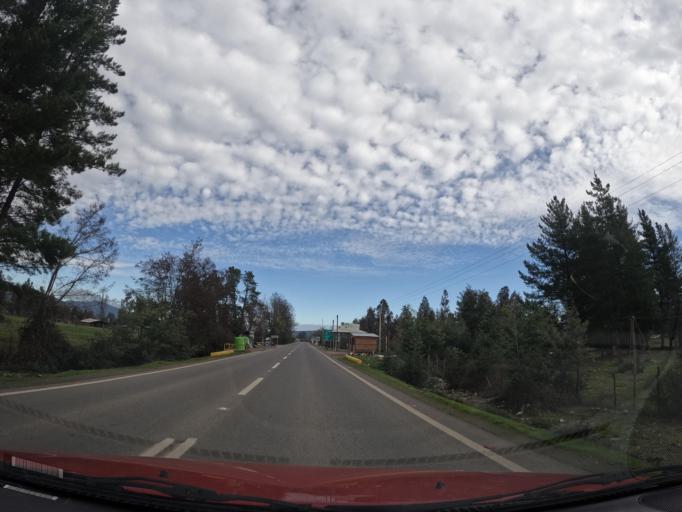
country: CL
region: Maule
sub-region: Provincia de Linares
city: Linares
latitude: -35.9102
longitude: -71.4917
